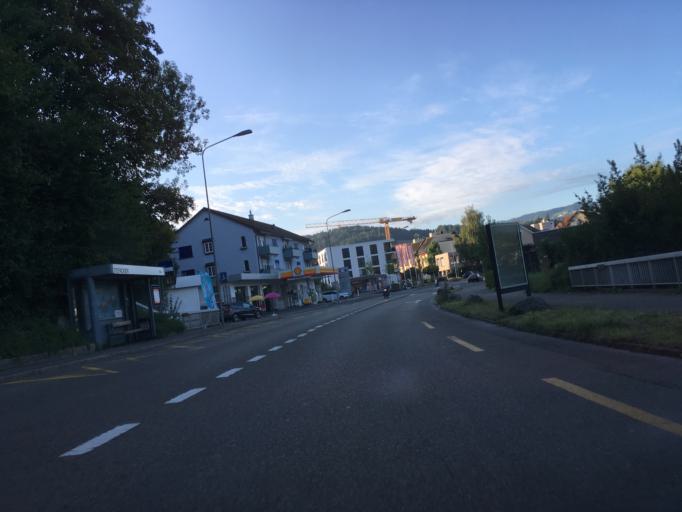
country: CH
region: Zurich
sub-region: Bezirk Horgen
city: Adliswil / Sood
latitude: 47.3167
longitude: 8.5299
